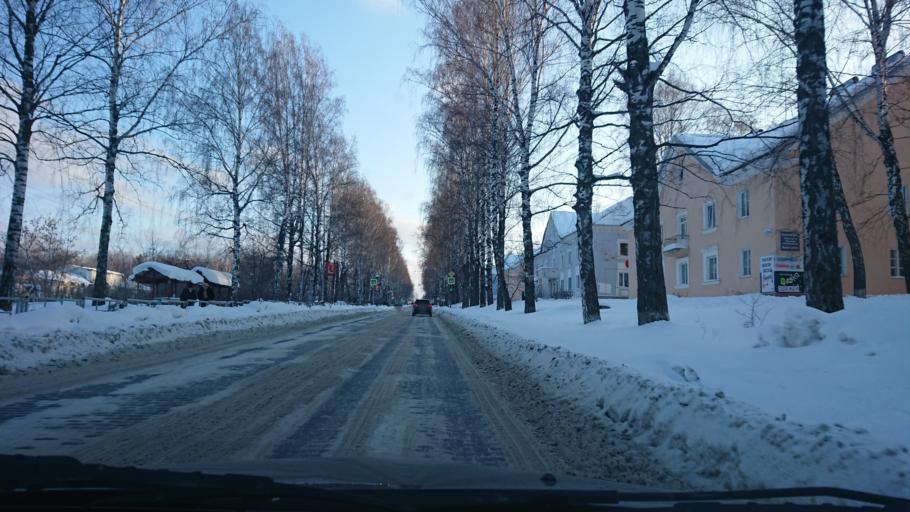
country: RU
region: Sverdlovsk
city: Degtyarsk
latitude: 56.6975
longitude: 60.0877
